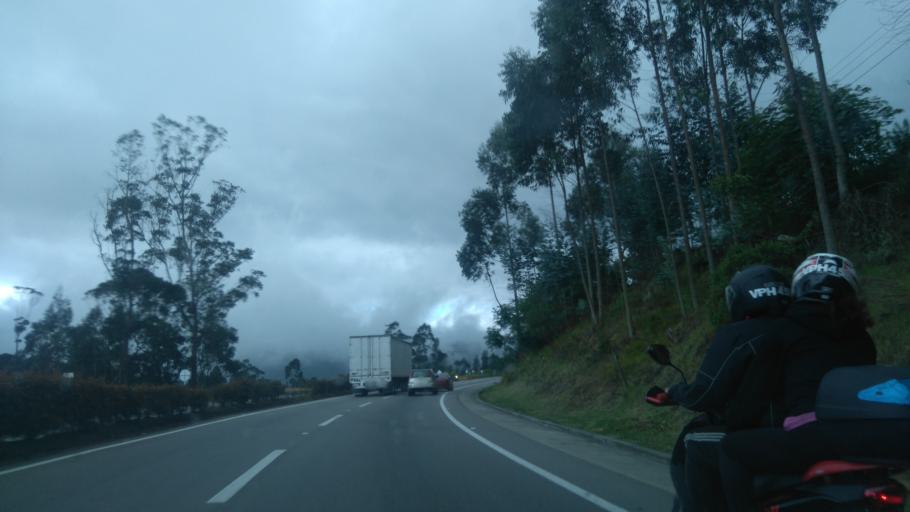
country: CO
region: Cundinamarca
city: El Rosal
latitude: 4.8903
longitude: -74.3028
